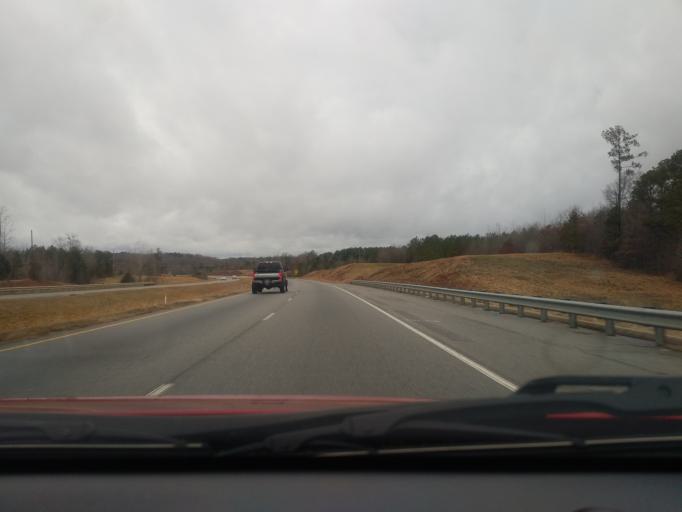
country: US
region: Georgia
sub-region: Henry County
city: Locust Grove
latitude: 33.2601
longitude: -84.1217
